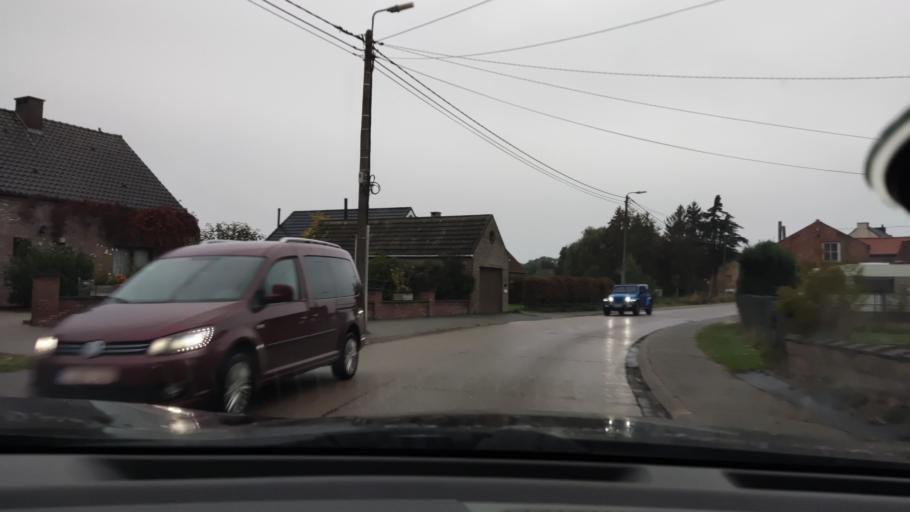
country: BE
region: Wallonia
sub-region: Province du Brabant Wallon
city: Beauvechain
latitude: 50.7605
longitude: 4.7846
